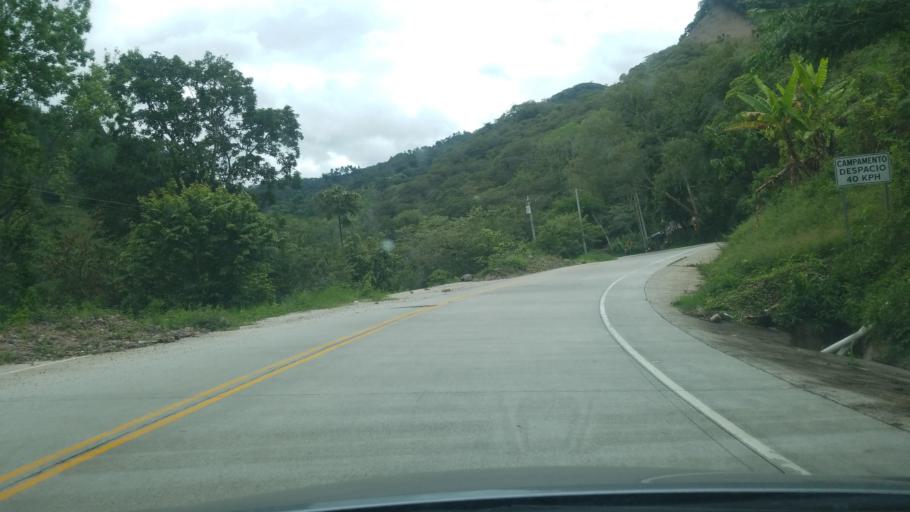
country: HN
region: Copan
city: San Jeronimo
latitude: 14.9325
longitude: -88.9534
